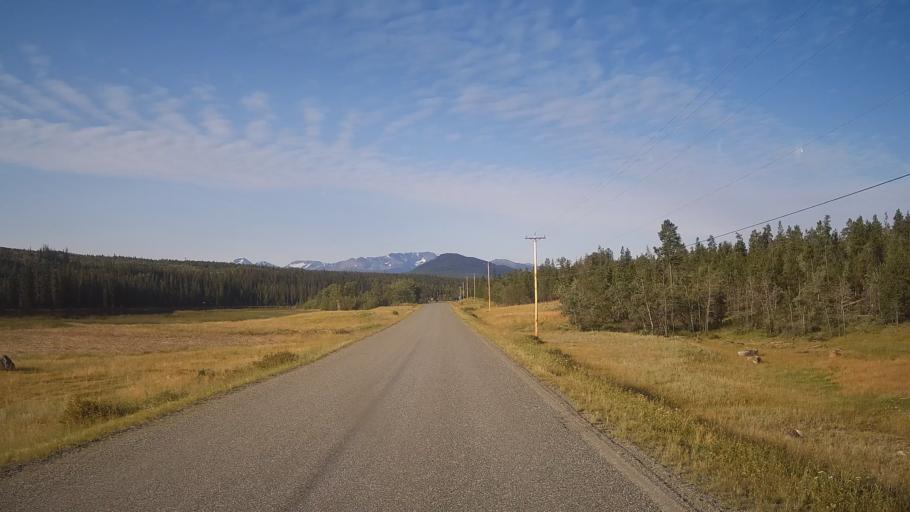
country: CA
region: British Columbia
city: Hanceville
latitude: 51.9447
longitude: -124.4590
